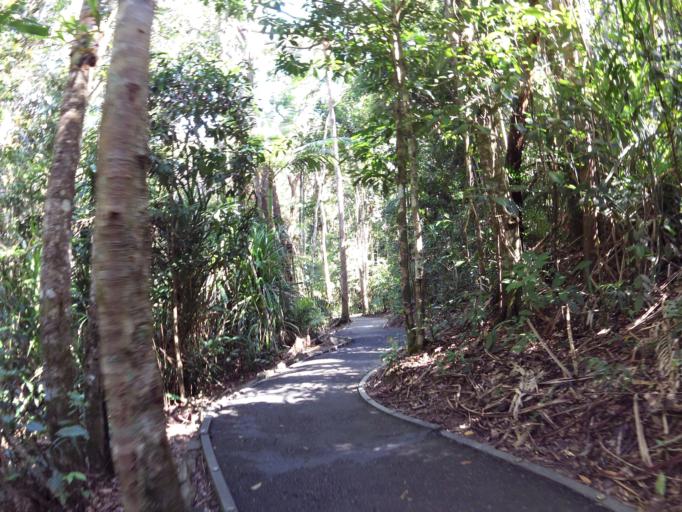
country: AU
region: Queensland
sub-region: Tablelands
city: Kuranda
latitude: -16.8219
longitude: 145.6346
